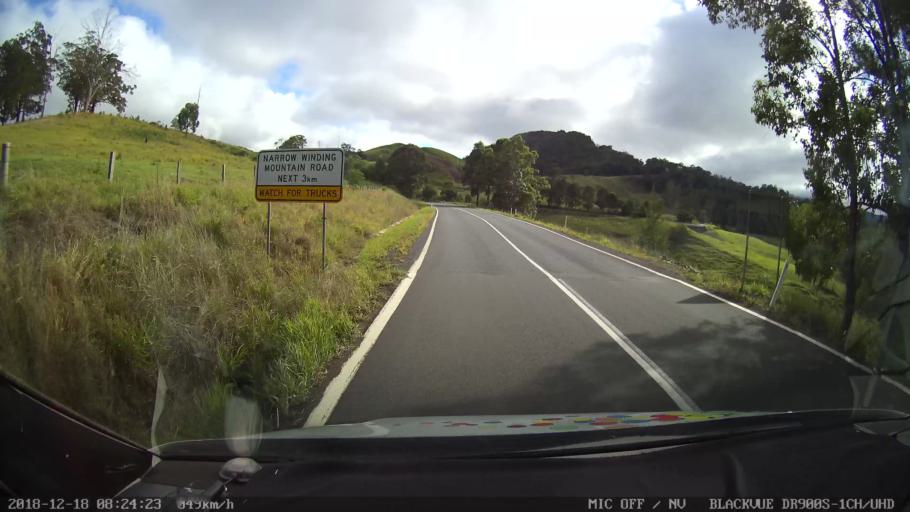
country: AU
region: New South Wales
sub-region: Kyogle
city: Kyogle
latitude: -28.3230
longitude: 152.7345
